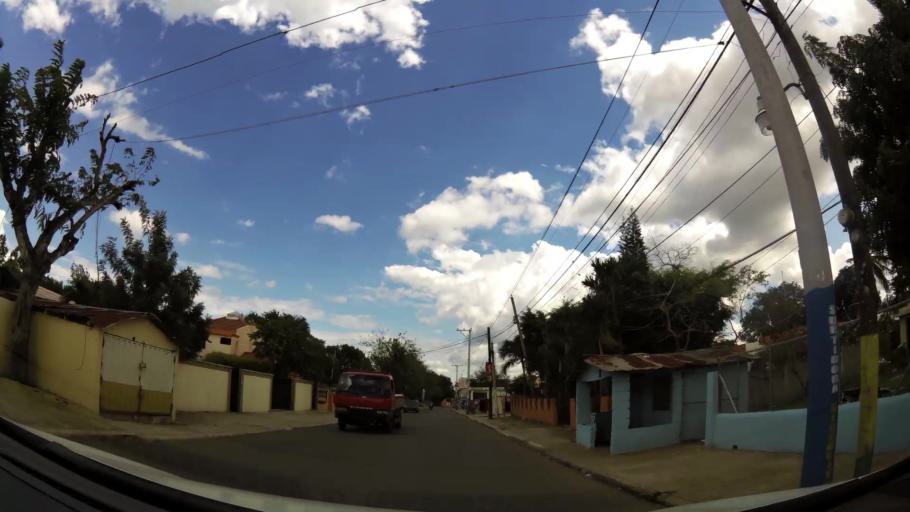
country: DO
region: Santiago
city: Licey al Medio
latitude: 19.3954
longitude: -70.6473
